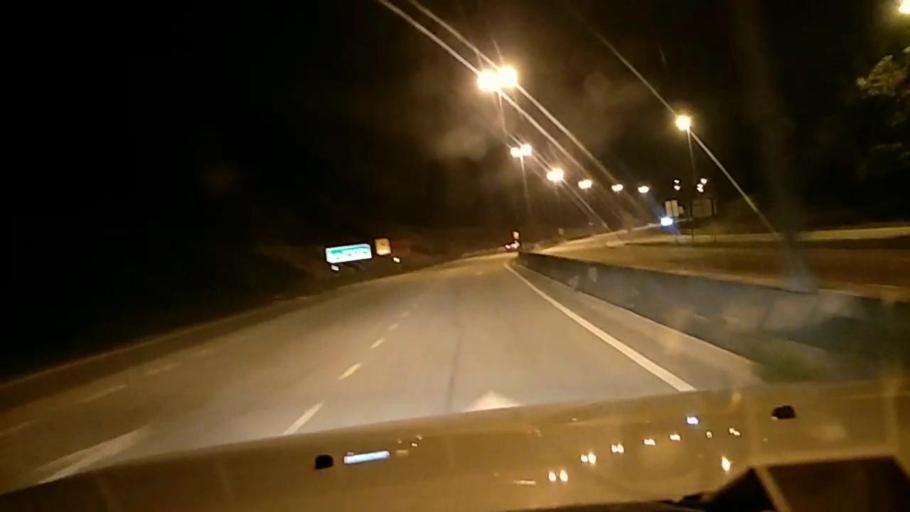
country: MY
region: Selangor
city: Kampung Baru Subang
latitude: 3.1329
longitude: 101.5026
